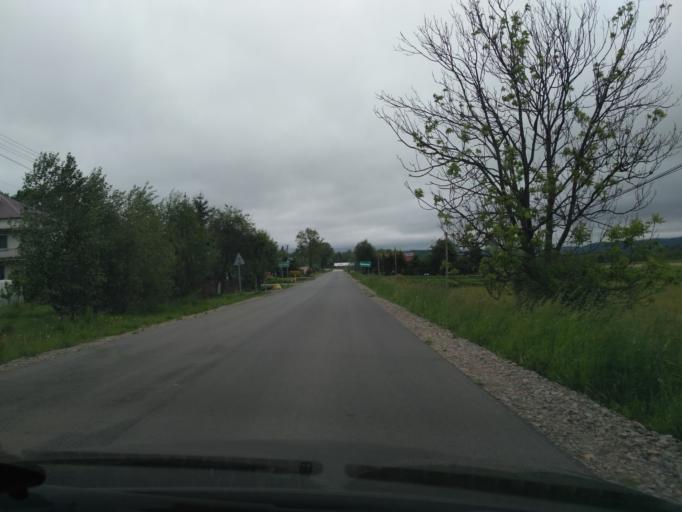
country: PL
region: Subcarpathian Voivodeship
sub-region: Powiat jasielski
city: Brzyska
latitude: 49.8320
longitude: 21.3939
